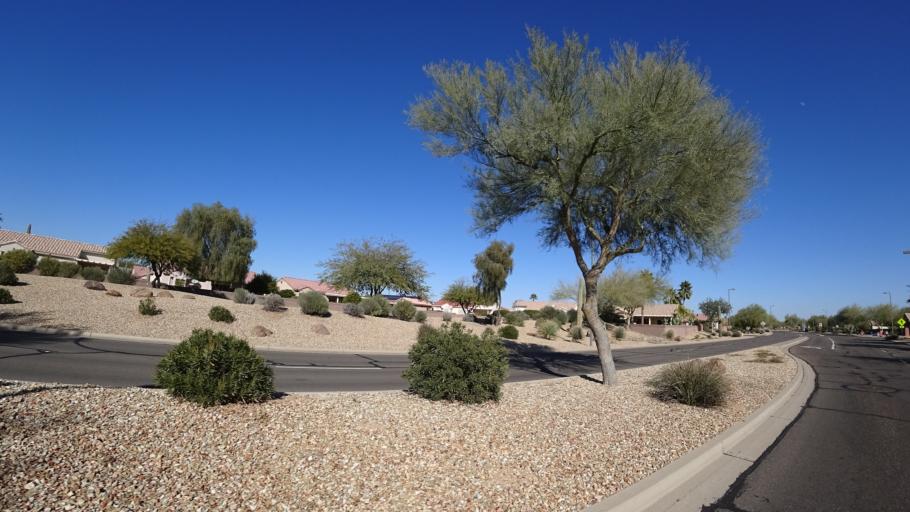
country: US
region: Arizona
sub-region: Maricopa County
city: Sun City West
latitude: 33.6688
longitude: -112.4039
